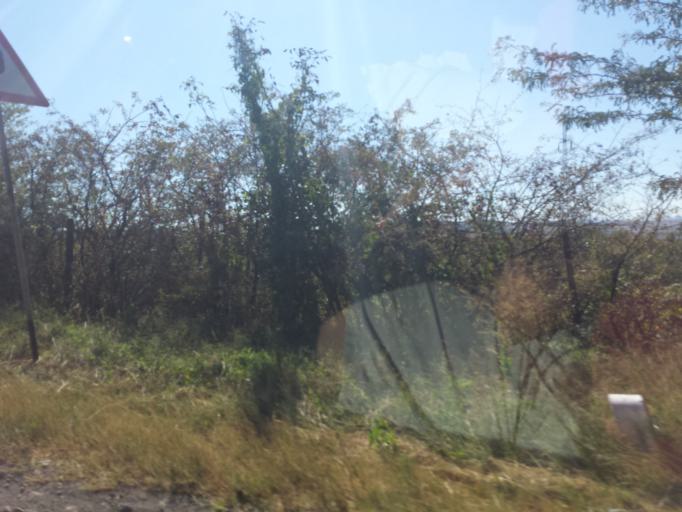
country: RO
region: Tulcea
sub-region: Municipiul Tulcea
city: Tulcea
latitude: 45.1543
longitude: 28.7856
